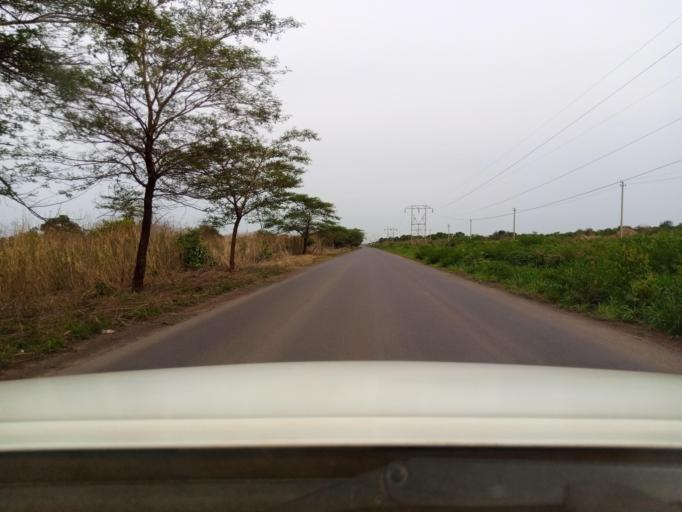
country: CD
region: Katanga
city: Likasi
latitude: -11.0149
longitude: 26.9195
